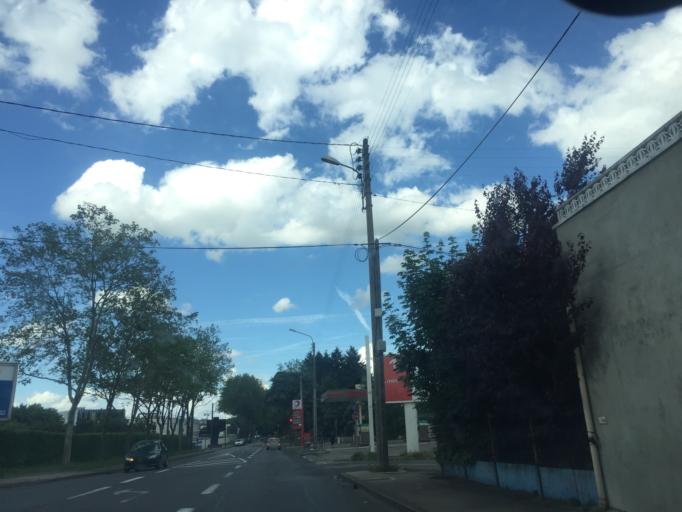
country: FR
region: Rhone-Alpes
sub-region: Departement du Rhone
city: Rillieux-la-Pape
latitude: 45.8131
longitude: 4.8874
